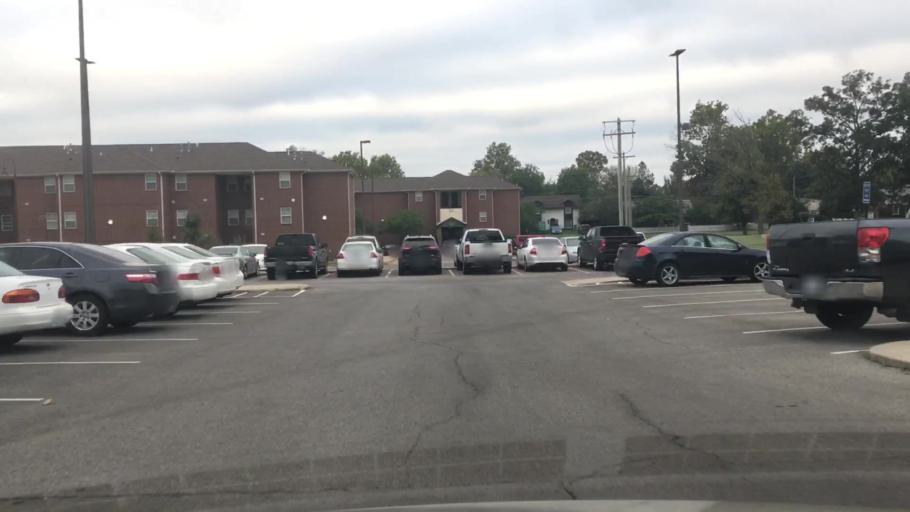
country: US
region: Oklahoma
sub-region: Cherokee County
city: Tahlequah
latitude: 35.9246
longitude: -94.9677
